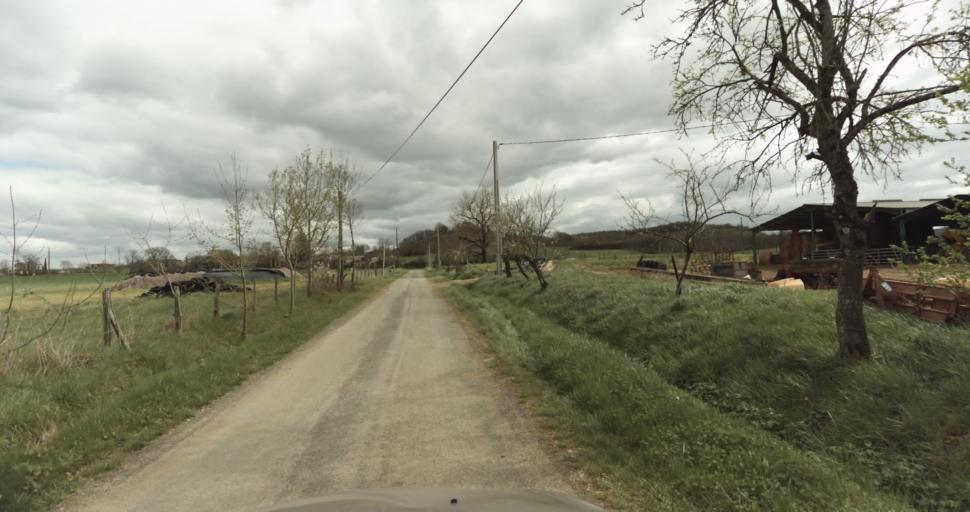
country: FR
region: Midi-Pyrenees
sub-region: Departement du Tarn
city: Puygouzon
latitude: 43.8870
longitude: 2.1803
